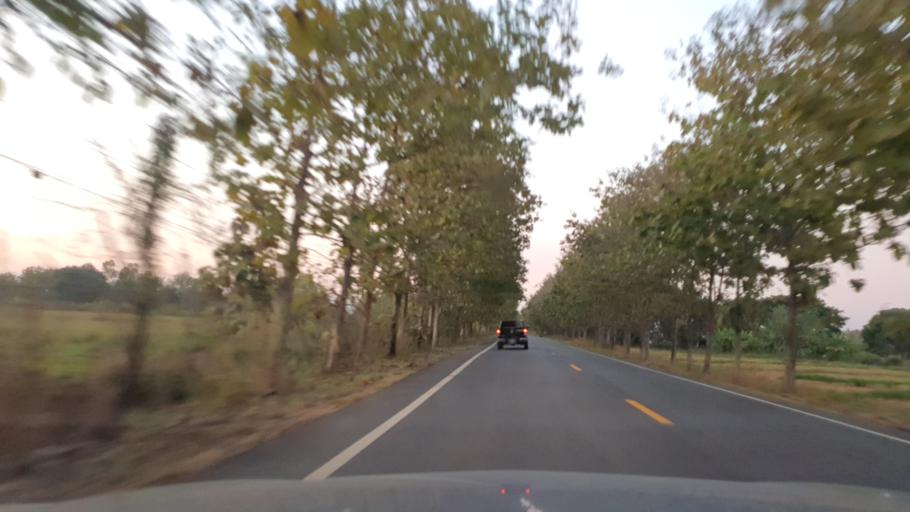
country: TH
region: Phayao
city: Dok Kham Tai
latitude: 19.1191
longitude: 100.0413
